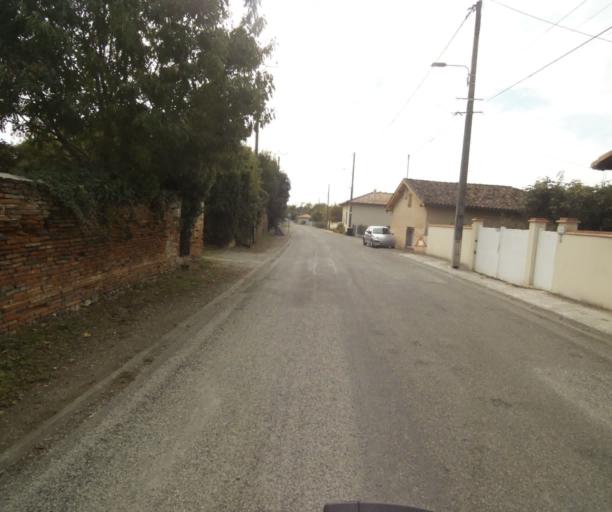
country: FR
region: Midi-Pyrenees
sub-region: Departement du Tarn-et-Garonne
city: Finhan
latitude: 43.9078
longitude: 1.2199
